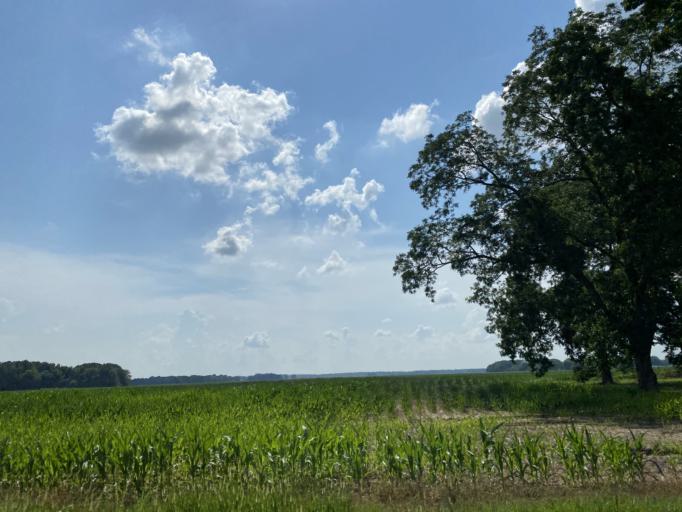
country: US
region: Alabama
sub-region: Lawrence County
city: Town Creek
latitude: 34.6702
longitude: -87.4060
